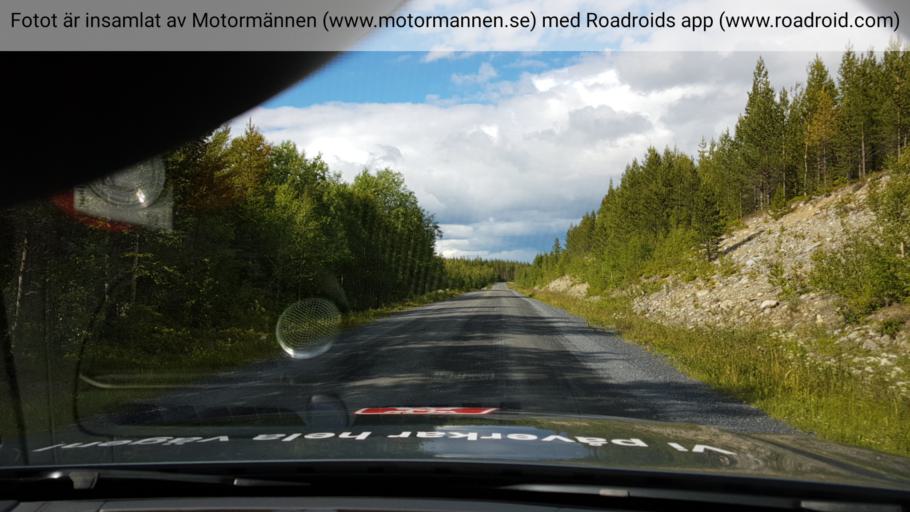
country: SE
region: Jaemtland
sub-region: Krokoms Kommun
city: Valla
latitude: 63.0673
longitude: 13.9589
